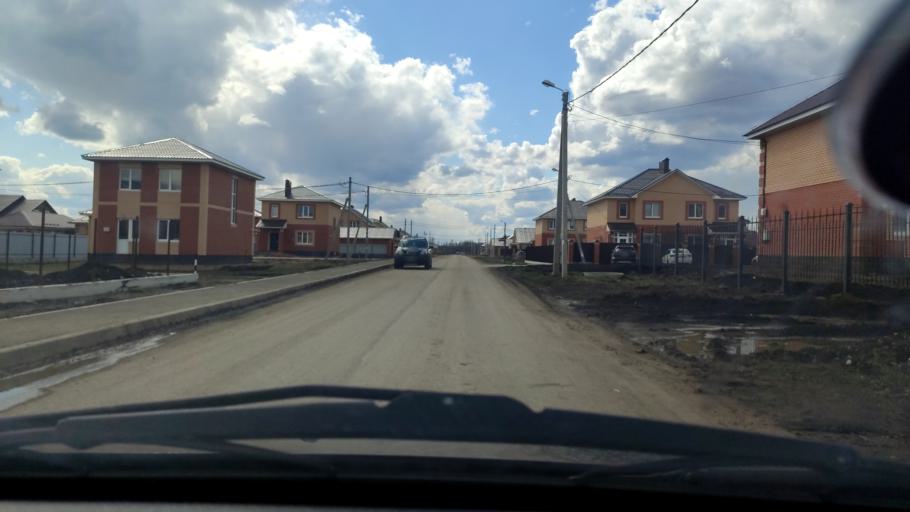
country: RU
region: Bashkortostan
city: Ufa
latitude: 54.6202
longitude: 55.8845
